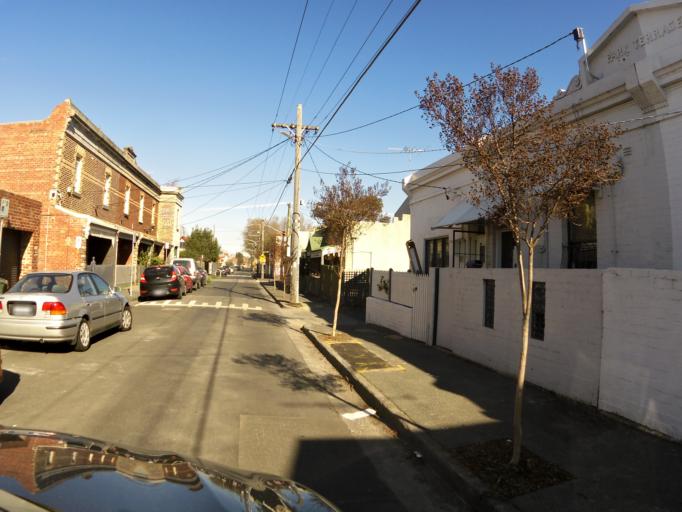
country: AU
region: Victoria
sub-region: Yarra
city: Clifton Hill
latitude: -37.8016
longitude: 144.9951
